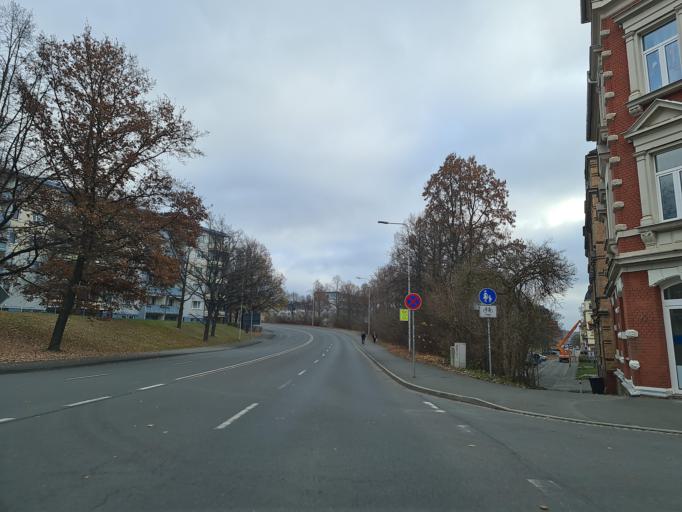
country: DE
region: Saxony
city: Plauen
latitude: 50.5010
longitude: 12.1299
